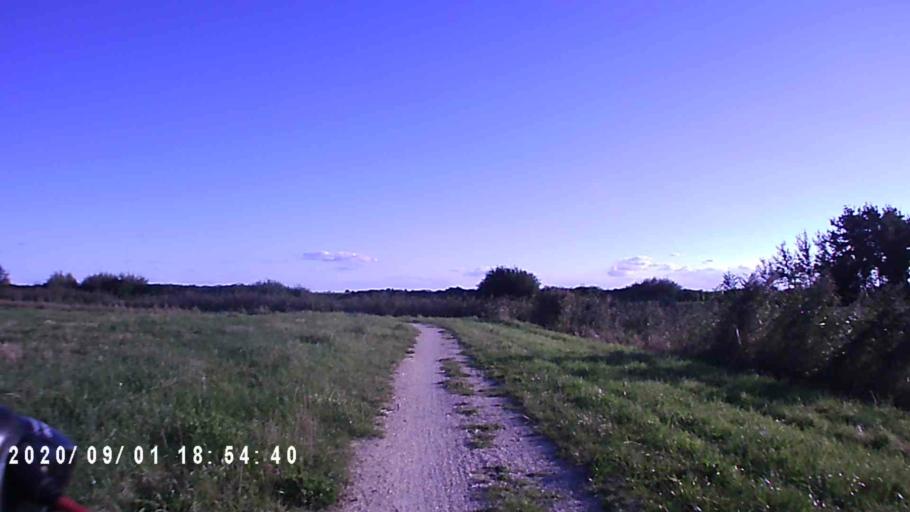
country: NL
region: Groningen
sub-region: Gemeente Veendam
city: Veendam
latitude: 53.1304
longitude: 6.8455
